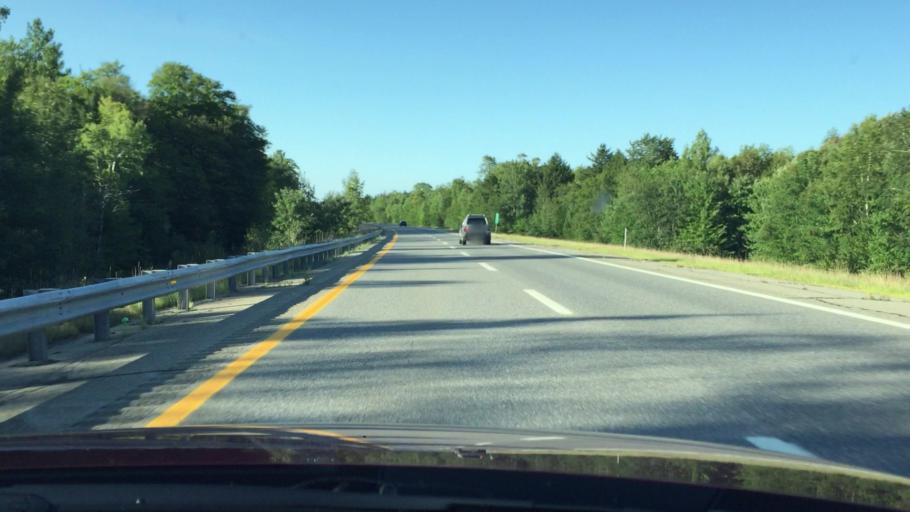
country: US
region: Maine
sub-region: Penobscot County
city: Lincoln
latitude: 45.4248
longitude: -68.5890
